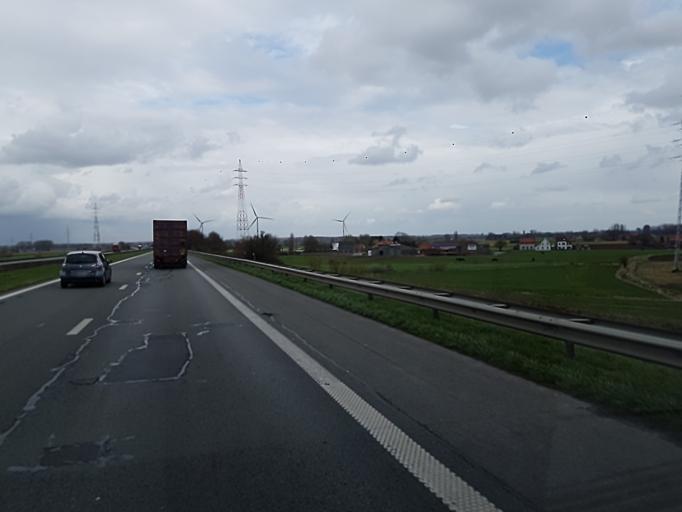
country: BE
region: Wallonia
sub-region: Province du Hainaut
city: Estaimpuis
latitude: 50.6768
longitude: 3.2905
